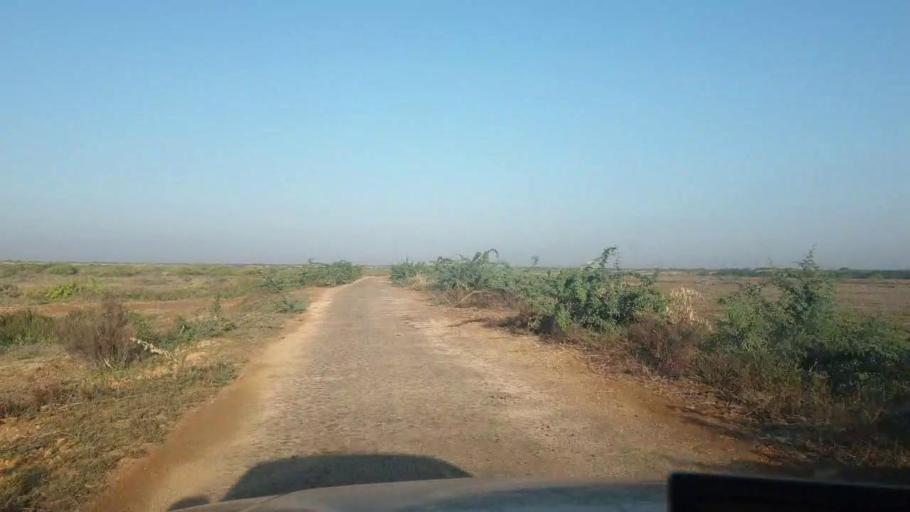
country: PK
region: Sindh
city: Thatta
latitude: 24.7022
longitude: 67.8508
